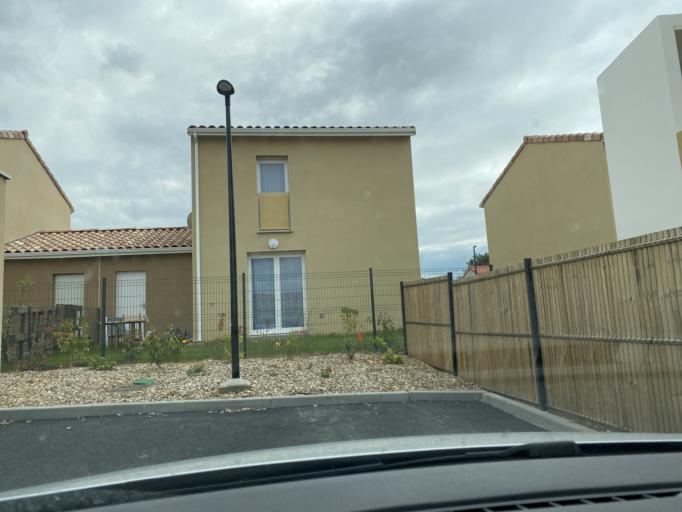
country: FR
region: Midi-Pyrenees
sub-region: Departement de la Haute-Garonne
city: Ayguesvives
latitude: 43.4285
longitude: 1.5942
